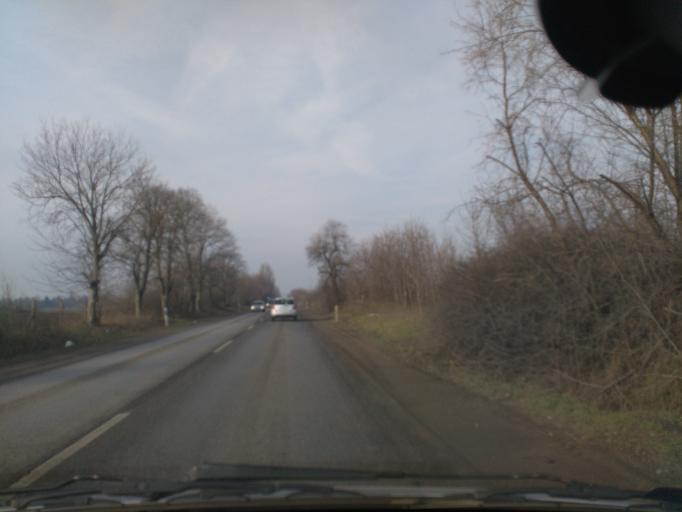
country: HU
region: Pest
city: Solymar
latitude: 47.6055
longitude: 18.9481
